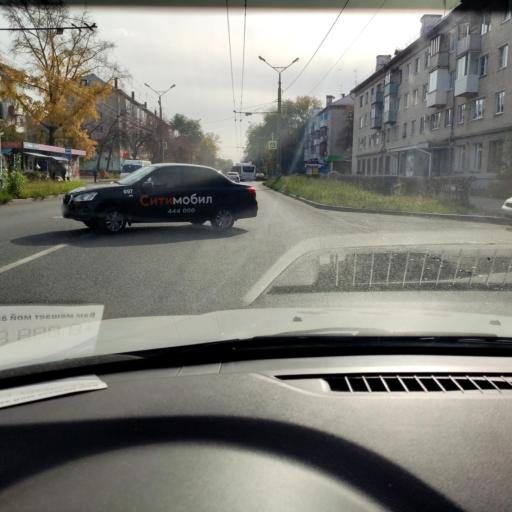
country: RU
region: Samara
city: Tol'yatti
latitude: 53.5182
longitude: 49.4161
